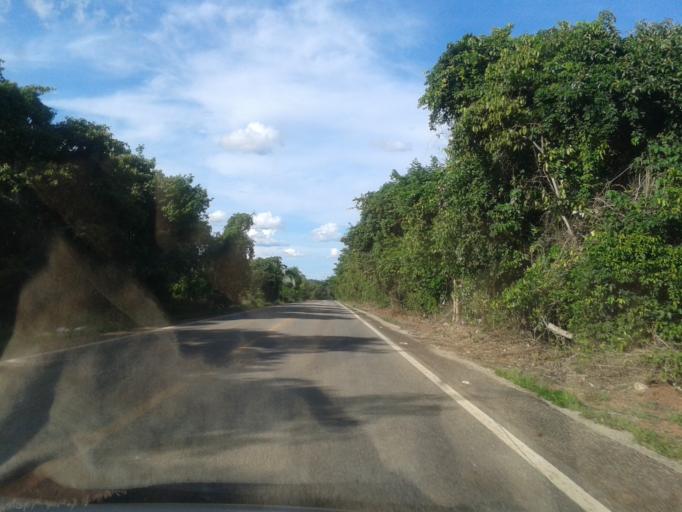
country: BR
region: Goias
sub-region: Mozarlandia
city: Mozarlandia
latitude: -14.4360
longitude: -50.4567
